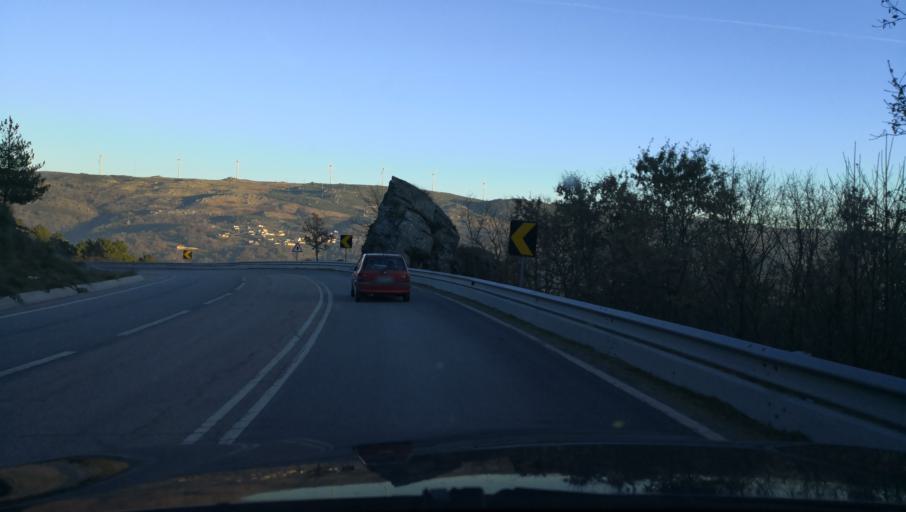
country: PT
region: Vila Real
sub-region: Vila Pouca de Aguiar
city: Vila Pouca de Aguiar
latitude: 41.4885
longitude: -7.6652
